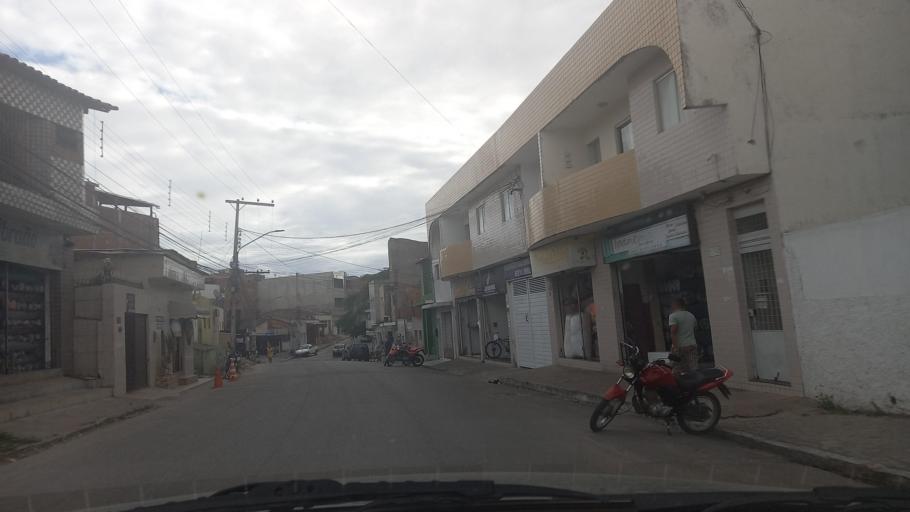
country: BR
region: Pernambuco
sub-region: Caruaru
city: Caruaru
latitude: -8.2936
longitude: -35.9754
